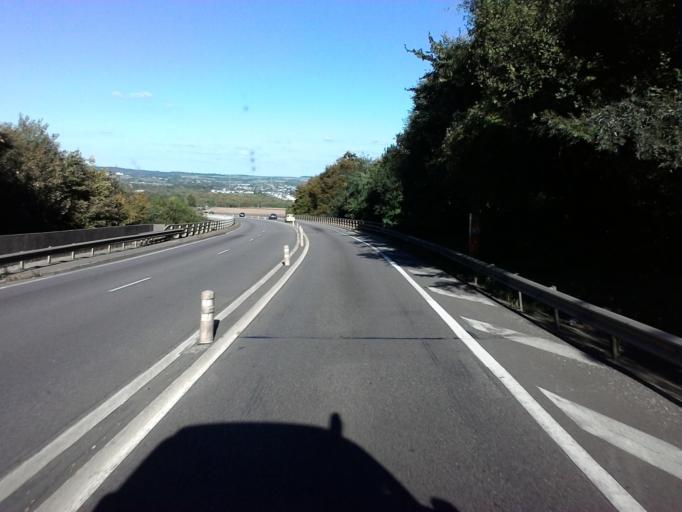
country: FR
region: Lorraine
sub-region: Departement de Meurthe-et-Moselle
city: Longwy
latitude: 49.5433
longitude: 5.7657
